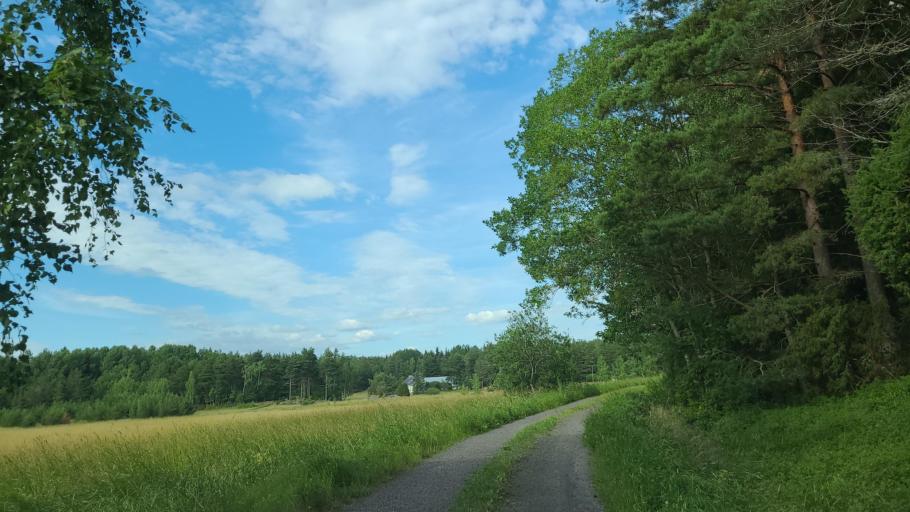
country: FI
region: Varsinais-Suomi
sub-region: Turku
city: Rymaettylae
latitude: 60.2903
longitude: 21.9670
